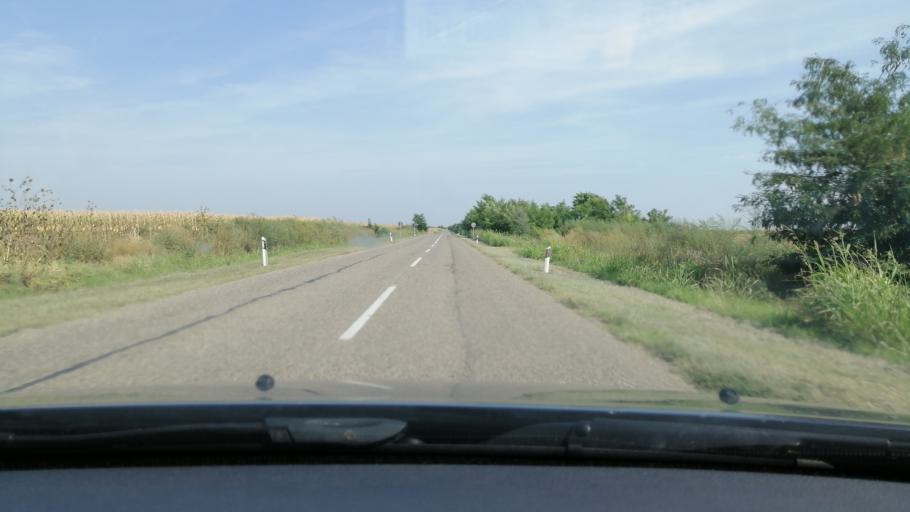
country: RS
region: Autonomna Pokrajina Vojvodina
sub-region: Juznobanatski Okrug
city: Kovacica
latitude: 45.1564
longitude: 20.6170
